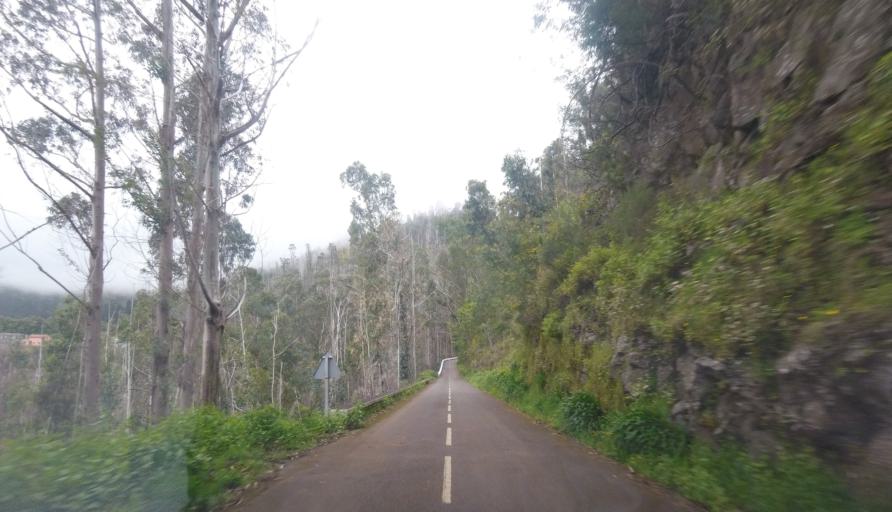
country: PT
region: Madeira
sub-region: Funchal
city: Nossa Senhora do Monte
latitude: 32.6879
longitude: -16.8895
